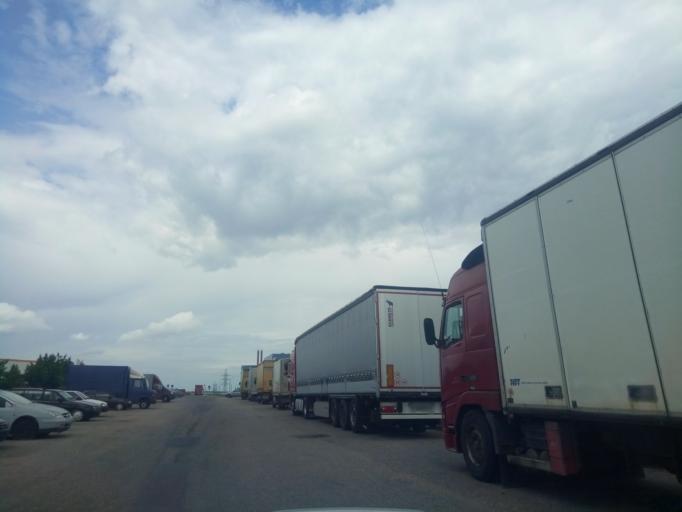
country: BY
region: Minsk
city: Zhdanovichy
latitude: 53.9347
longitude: 27.4209
